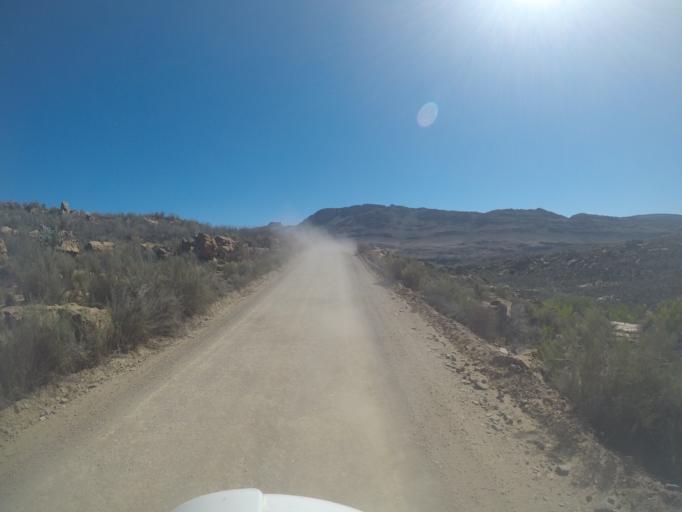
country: ZA
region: Western Cape
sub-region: West Coast District Municipality
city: Clanwilliam
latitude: -32.5060
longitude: 19.2826
